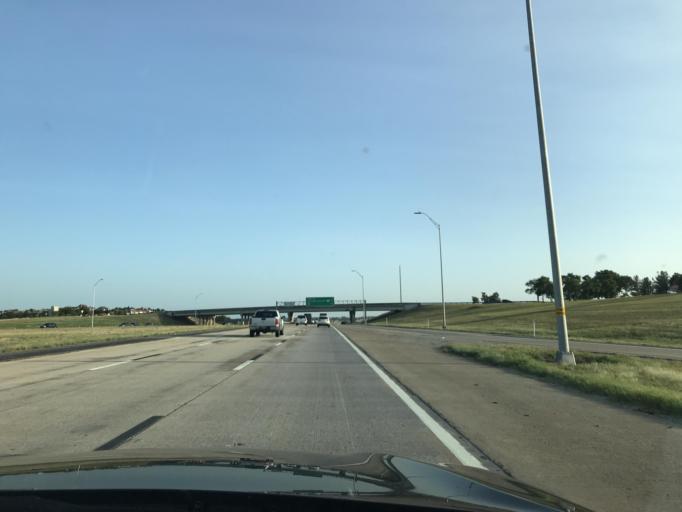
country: US
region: Texas
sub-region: Tarrant County
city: Benbrook
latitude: 32.6999
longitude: -97.4716
